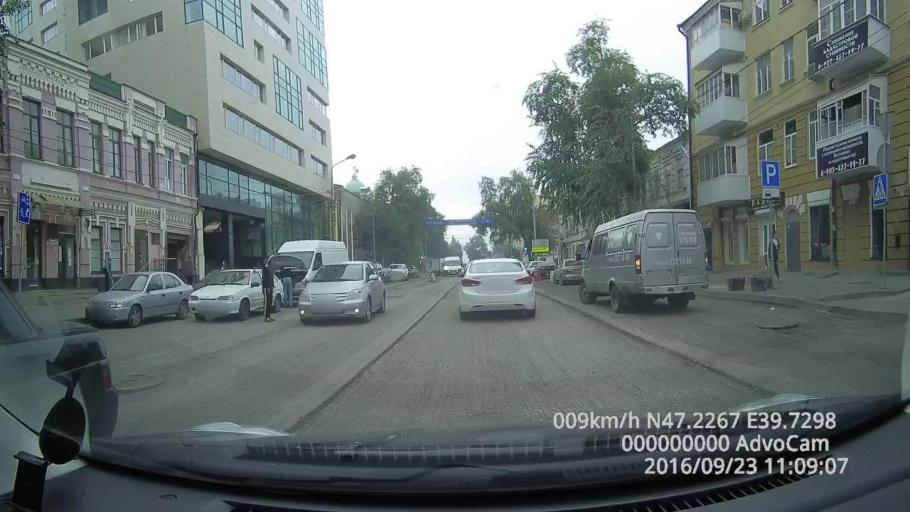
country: RU
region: Rostov
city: Rostov-na-Donu
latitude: 47.2265
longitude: 39.7299
